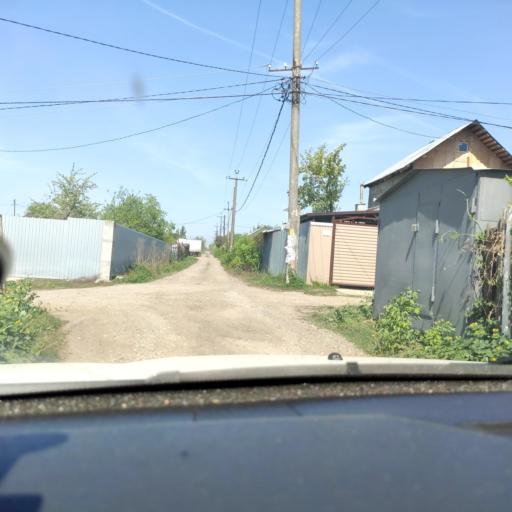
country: RU
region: Samara
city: Petra-Dubrava
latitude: 53.2774
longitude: 50.3286
